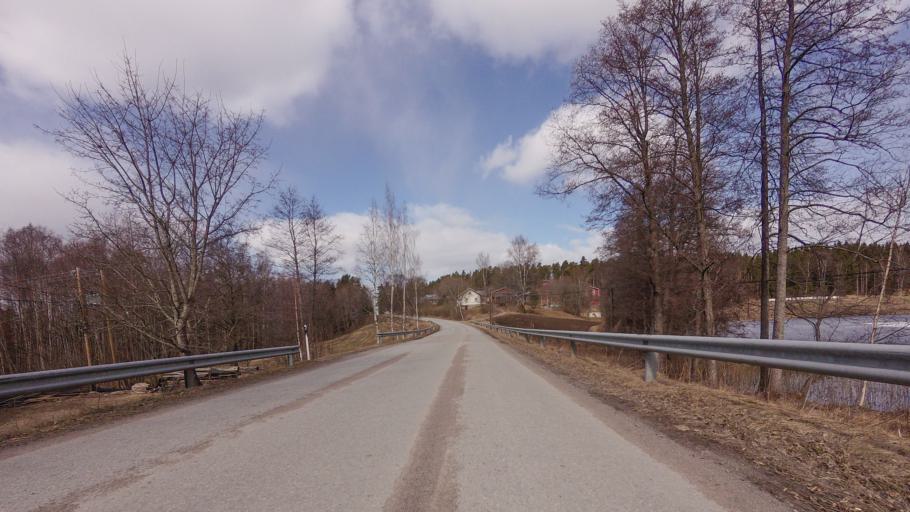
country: FI
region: Uusimaa
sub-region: Helsinki
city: Karjalohja
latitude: 60.2644
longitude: 23.6723
